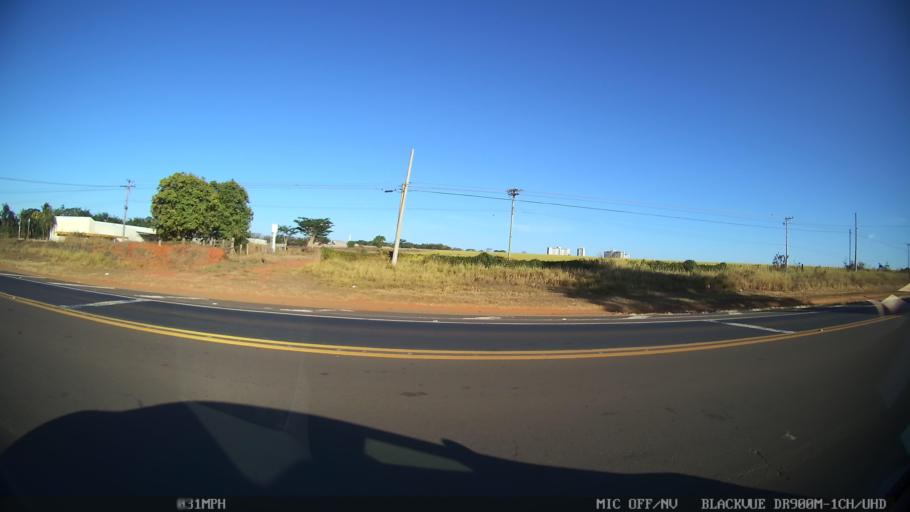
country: BR
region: Sao Paulo
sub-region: Olimpia
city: Olimpia
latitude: -20.6923
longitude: -48.9211
